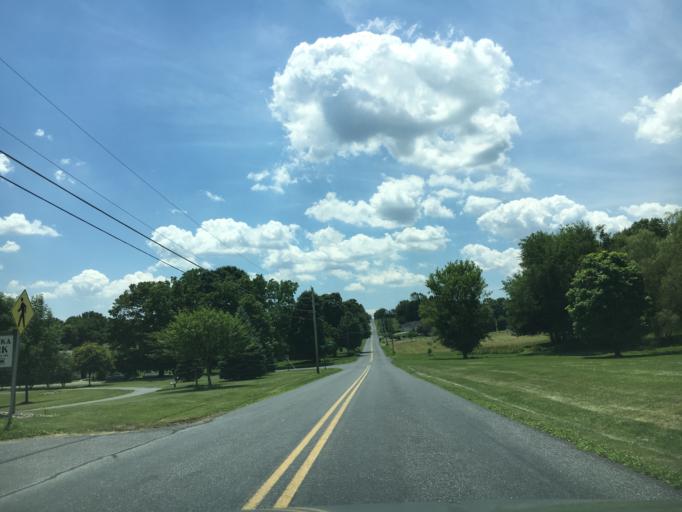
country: US
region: Pennsylvania
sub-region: Lehigh County
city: Schnecksville
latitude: 40.6662
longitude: -75.5753
